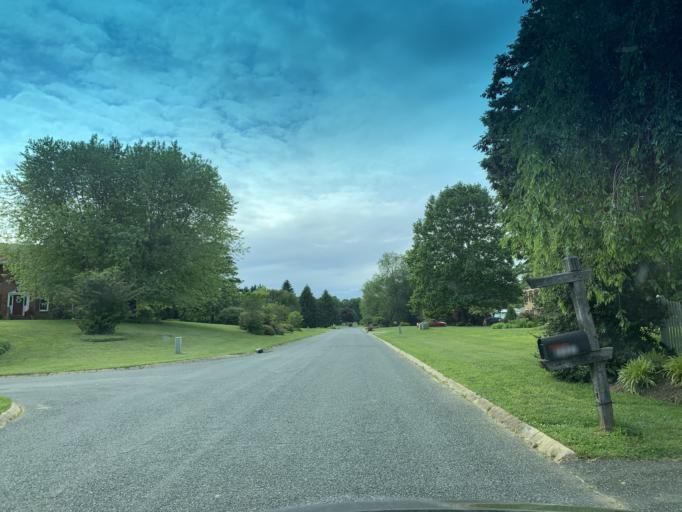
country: US
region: Maryland
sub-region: Harford County
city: Jarrettsville
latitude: 39.5983
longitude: -76.4630
